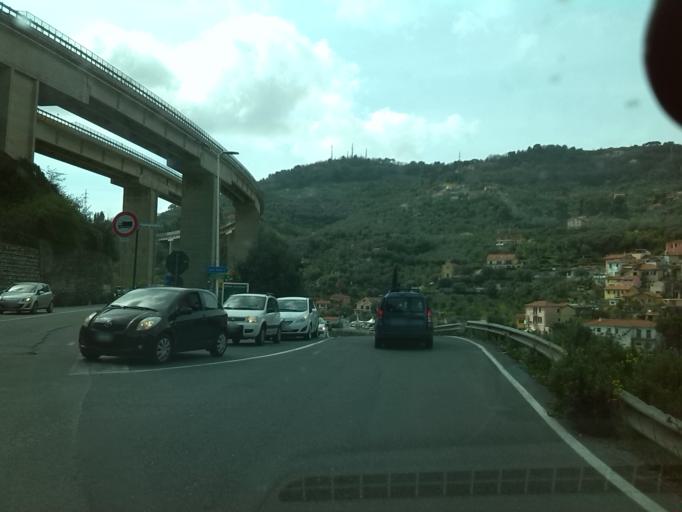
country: IT
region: Liguria
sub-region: Provincia di Imperia
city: Imperia
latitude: 43.9048
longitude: 8.0272
